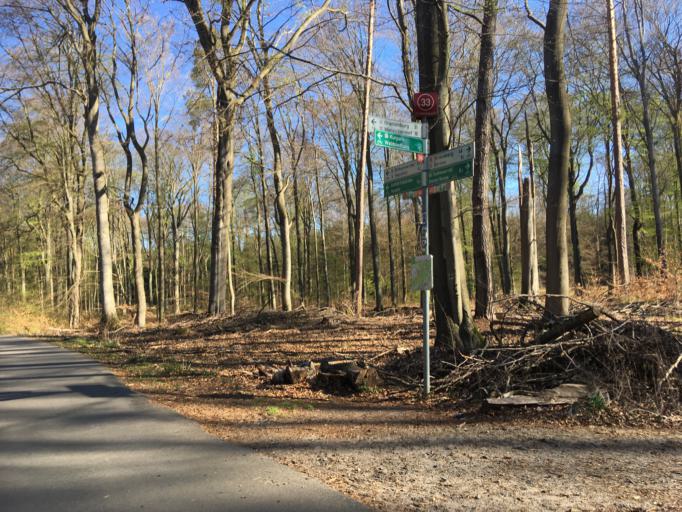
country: DE
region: Brandenburg
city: Wandlitz
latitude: 52.7290
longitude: 13.5088
